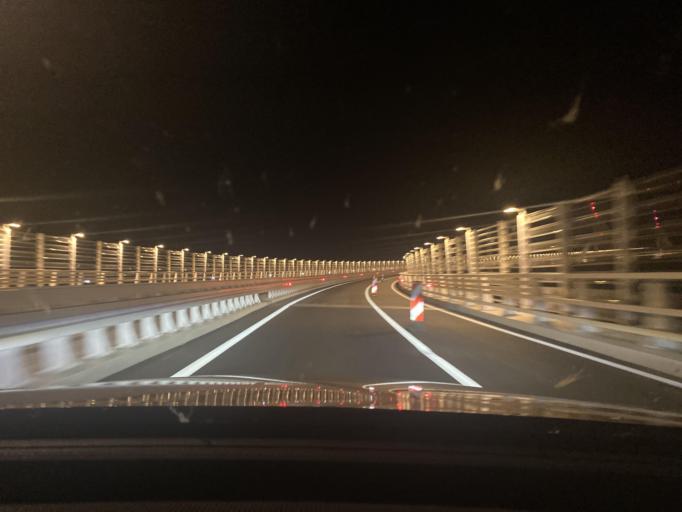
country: BA
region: Federation of Bosnia and Herzegovina
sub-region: Hercegovacko-Bosanski Kanton
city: Neum
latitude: 42.9411
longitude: 17.5433
